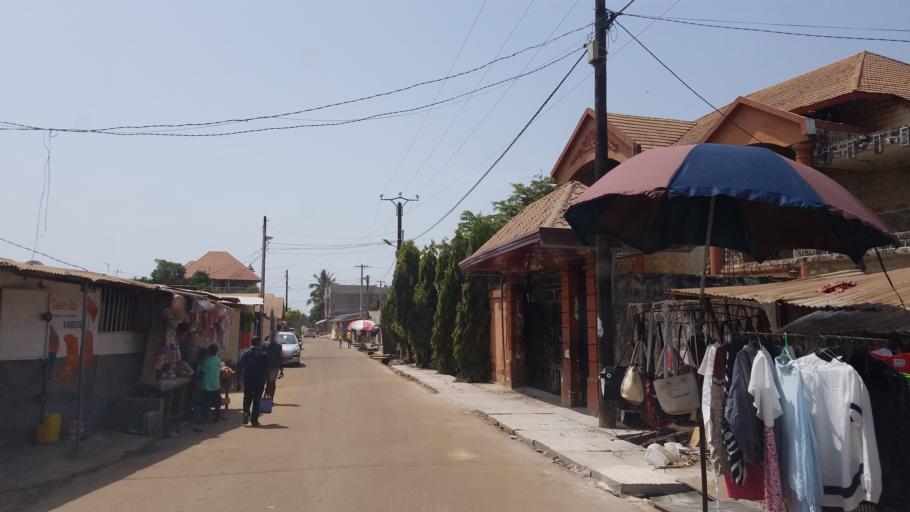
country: GN
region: Conakry
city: Conakry
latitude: 9.5791
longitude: -13.6615
